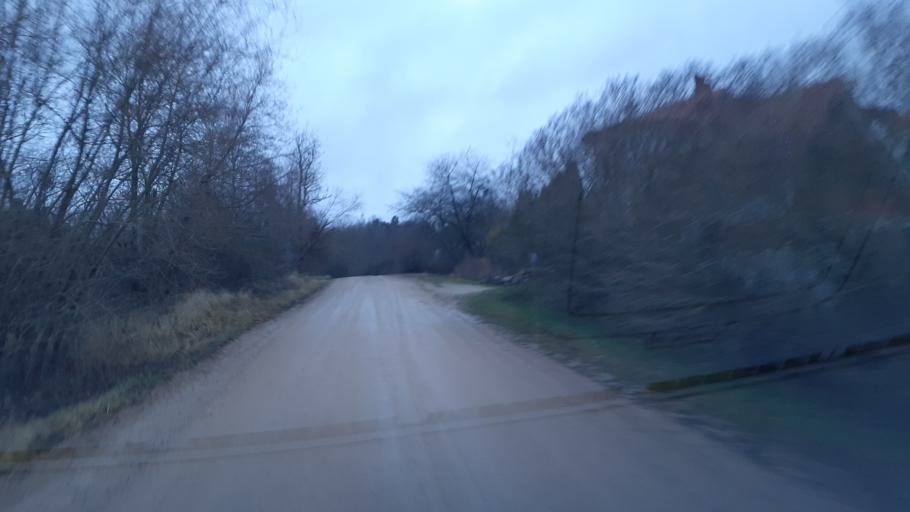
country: LV
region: Kuldigas Rajons
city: Kuldiga
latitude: 56.9882
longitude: 22.0487
